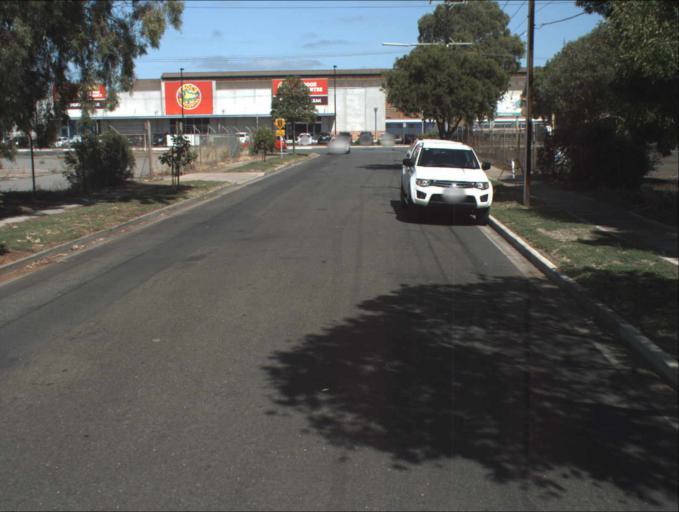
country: AU
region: South Australia
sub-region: Prospect
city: Prospect
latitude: -34.8698
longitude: 138.5847
